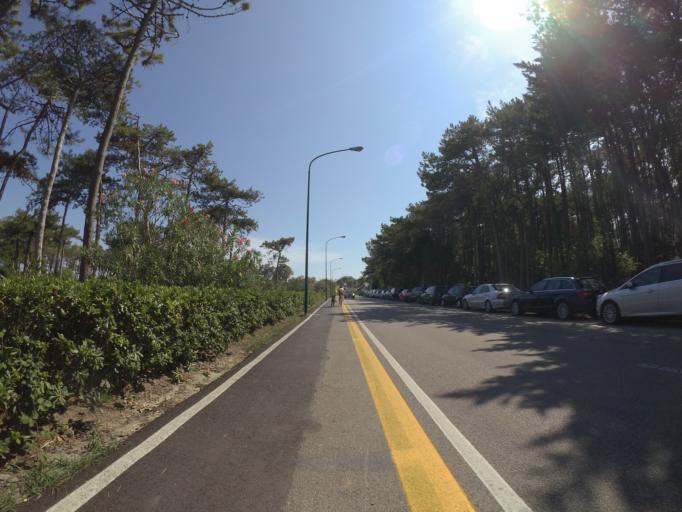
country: IT
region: Friuli Venezia Giulia
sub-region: Provincia di Udine
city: Lignano Sabbiadoro
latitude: 45.6592
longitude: 13.1043
